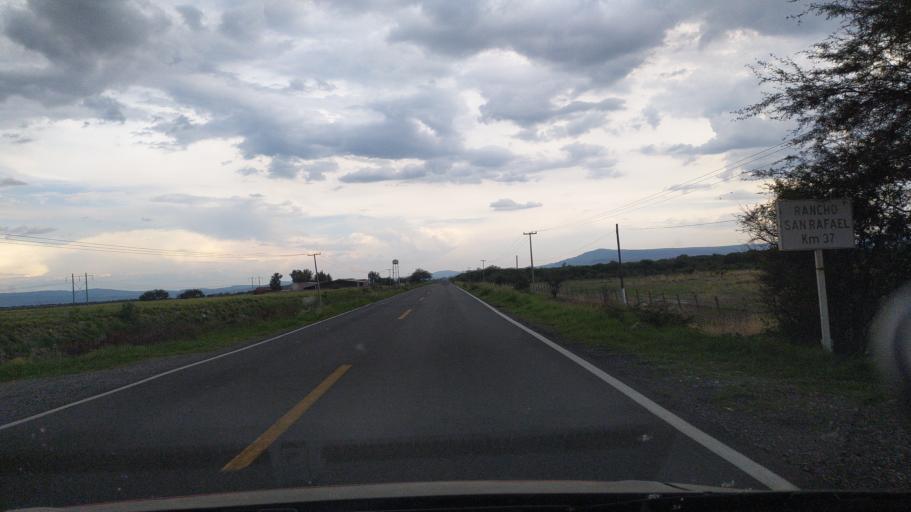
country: MX
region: Guanajuato
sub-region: San Francisco del Rincon
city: San Ignacio de Hidalgo
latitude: 20.8480
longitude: -101.8953
